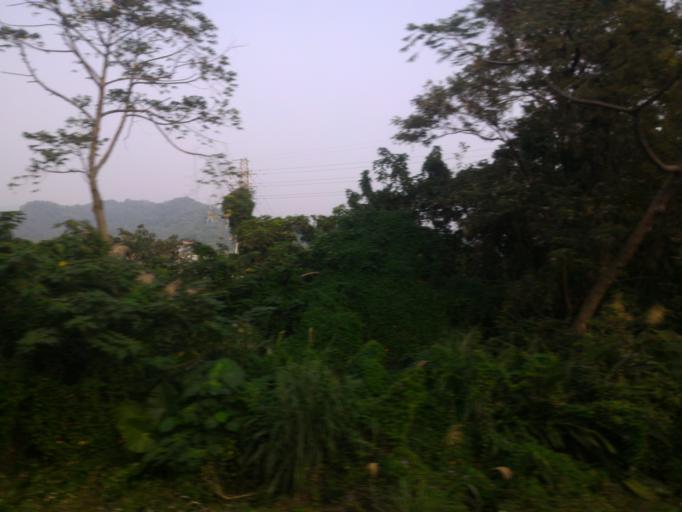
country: TW
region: Taiwan
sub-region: Taoyuan
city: Taoyuan
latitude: 24.9601
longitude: 121.3390
